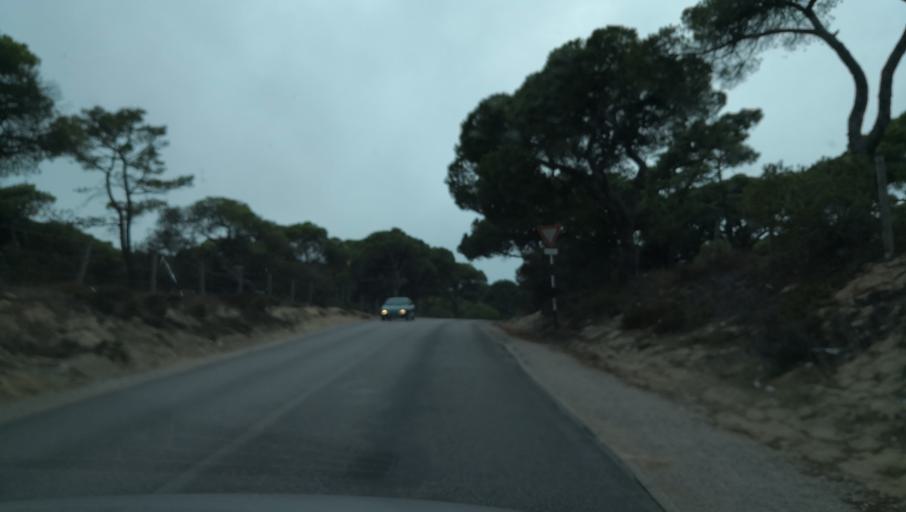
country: PT
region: Setubal
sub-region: Almada
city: Charneca
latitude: 38.5761
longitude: -9.1894
